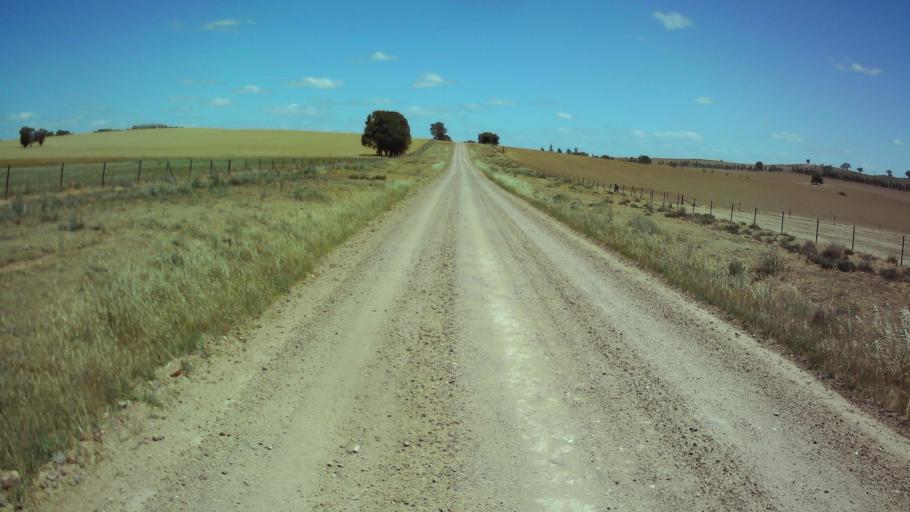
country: AU
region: New South Wales
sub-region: Weddin
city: Grenfell
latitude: -33.9454
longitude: 148.3294
